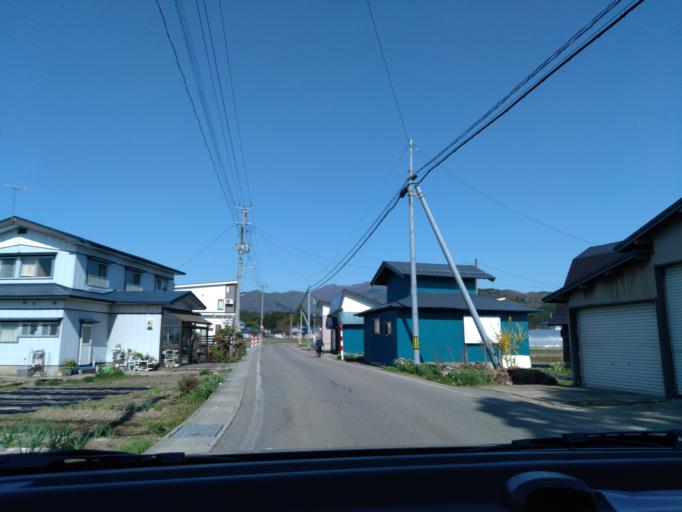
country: JP
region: Akita
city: Omagari
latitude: 39.4161
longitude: 140.5773
